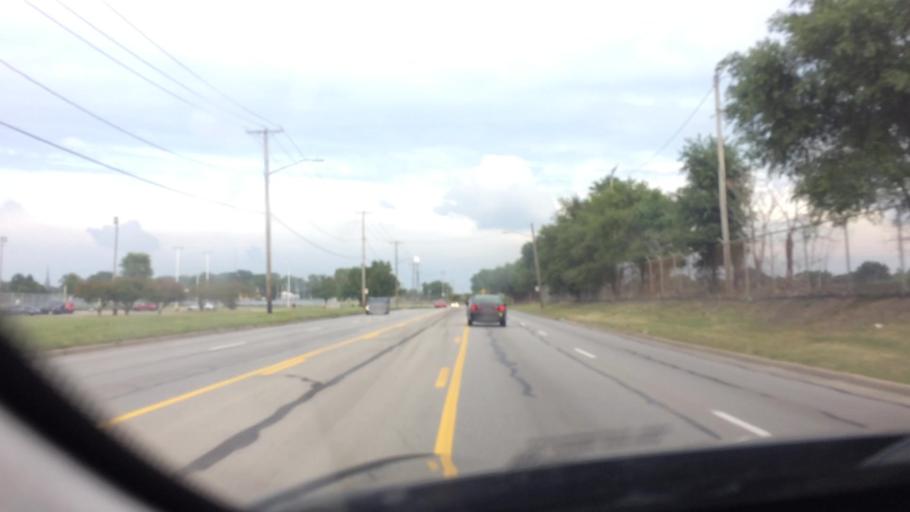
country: US
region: Ohio
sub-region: Wood County
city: Rossford
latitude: 41.6380
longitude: -83.5979
